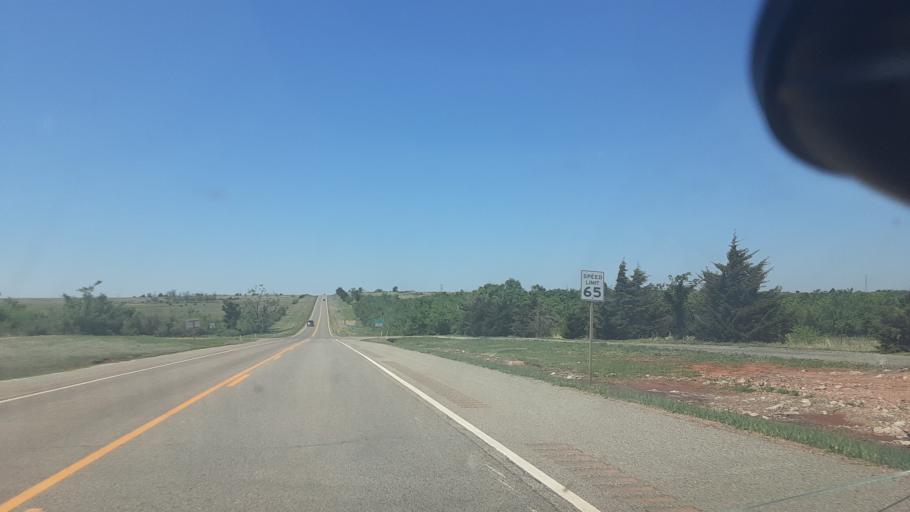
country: US
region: Oklahoma
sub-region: Noble County
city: Perry
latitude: 36.1157
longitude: -97.3525
